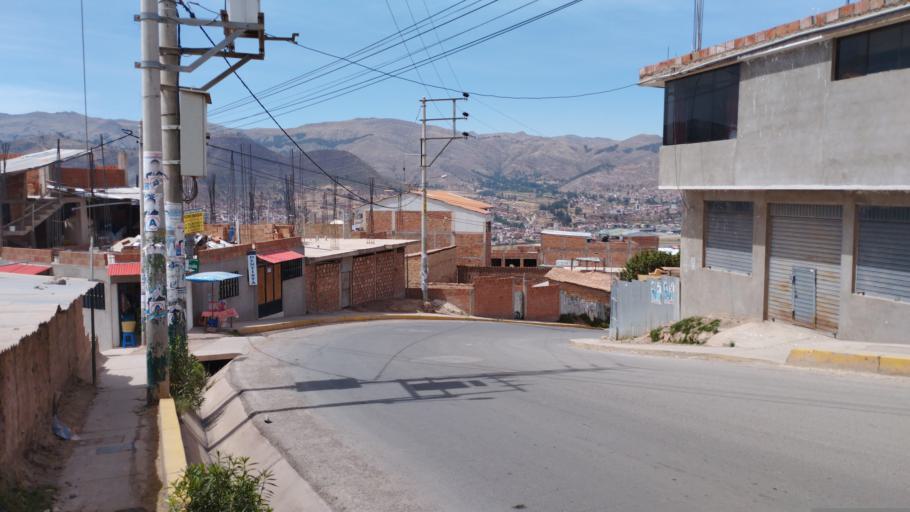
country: PE
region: Cusco
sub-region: Provincia de Cusco
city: Cusco
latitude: -13.5237
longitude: -71.9278
